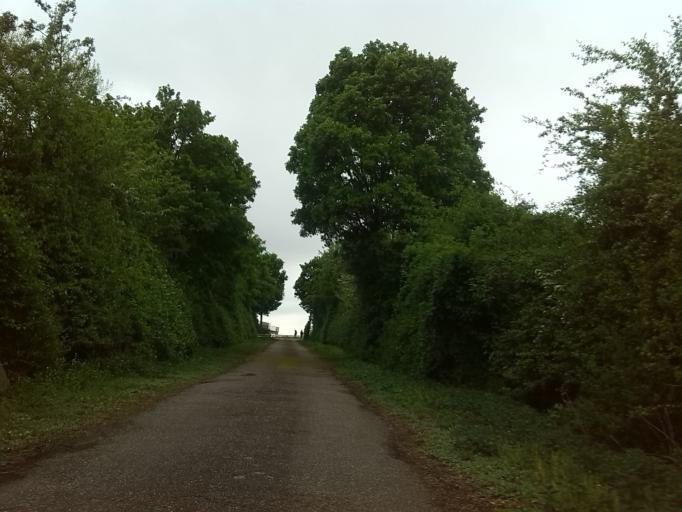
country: DE
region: Baden-Wuerttemberg
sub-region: Karlsruhe Region
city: Ilvesheim
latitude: 49.4658
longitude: 8.5292
